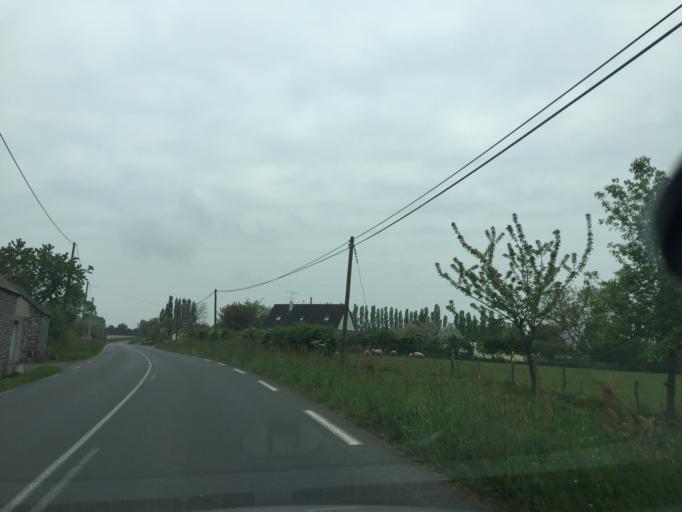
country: FR
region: Brittany
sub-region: Departement des Cotes-d'Armor
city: Matignon
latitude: 48.5854
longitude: -2.3220
